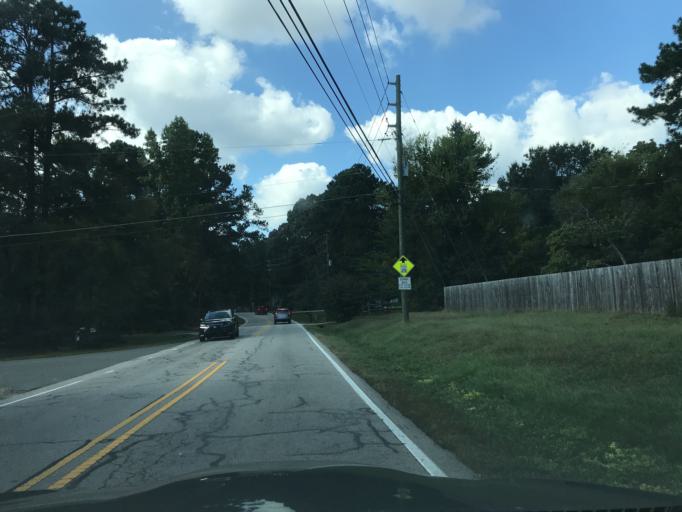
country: US
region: North Carolina
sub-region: Wake County
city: Rolesville
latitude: 35.8705
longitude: -78.5482
